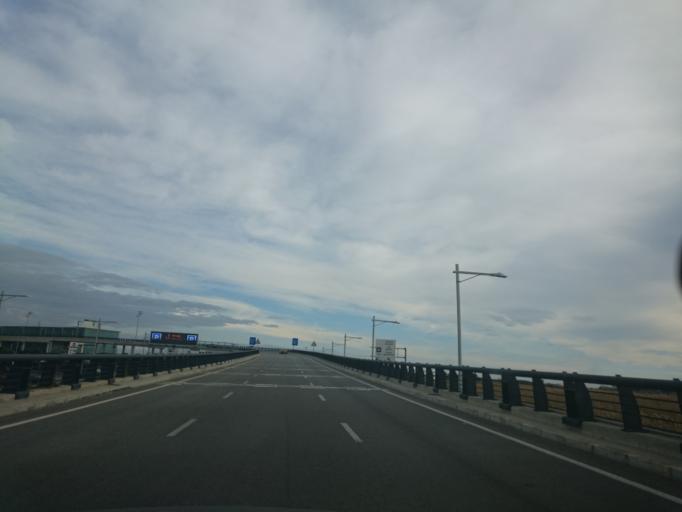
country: ES
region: Catalonia
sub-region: Provincia de Barcelona
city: El Prat de Llobregat
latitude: 41.2867
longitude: 2.0683
